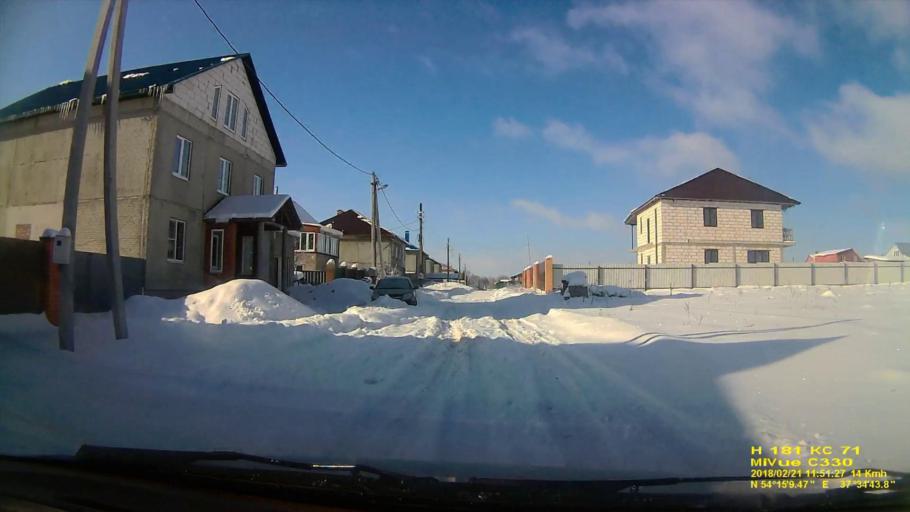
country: RU
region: Tula
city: Gorelki
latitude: 54.2526
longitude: 37.5786
